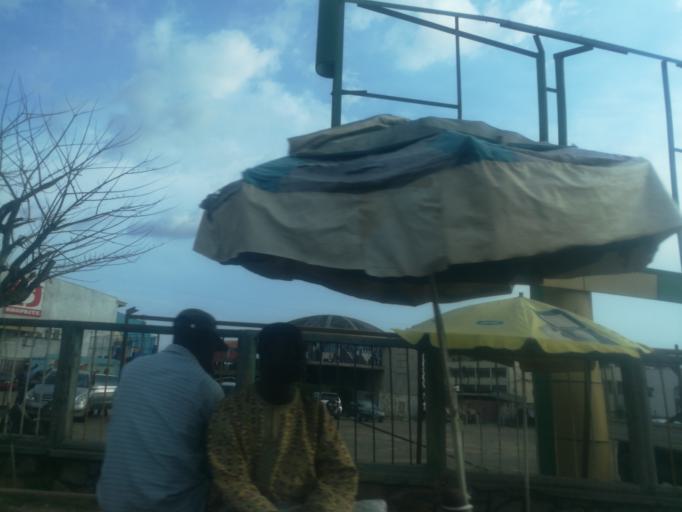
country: NG
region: Oyo
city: Ibadan
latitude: 7.3880
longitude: 3.8781
